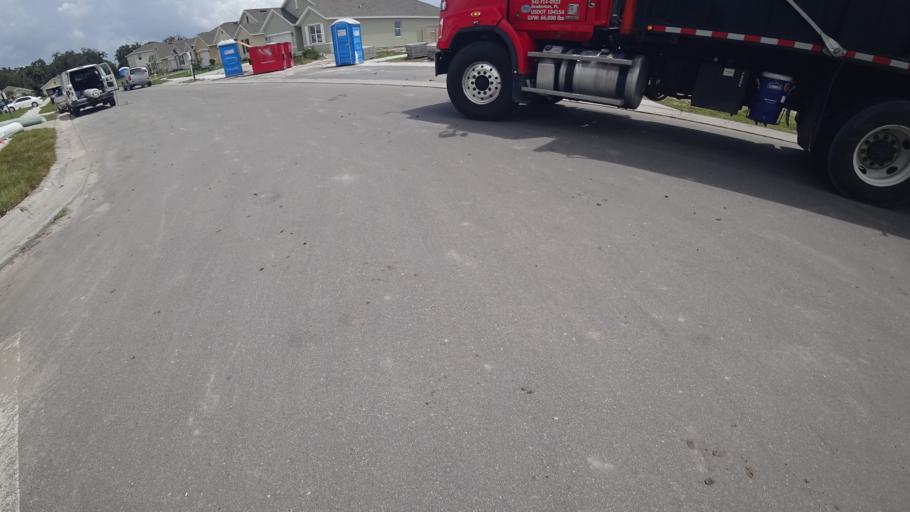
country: US
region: Florida
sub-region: Manatee County
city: Ellenton
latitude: 27.5491
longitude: -82.5152
